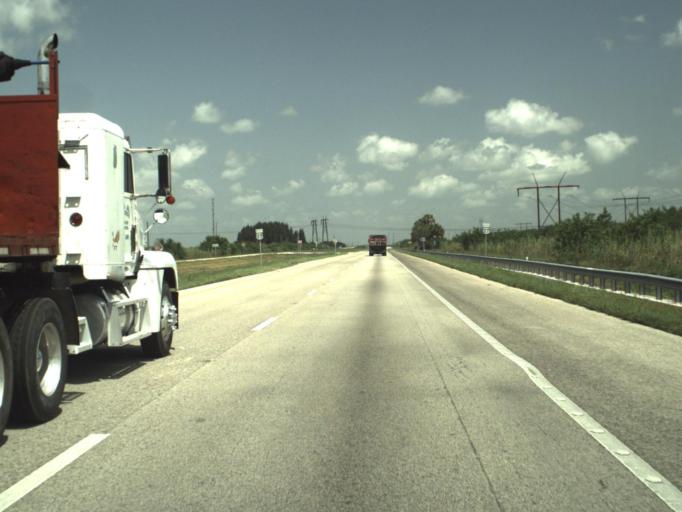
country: US
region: Florida
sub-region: Broward County
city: Weston
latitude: 26.3288
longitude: -80.5330
